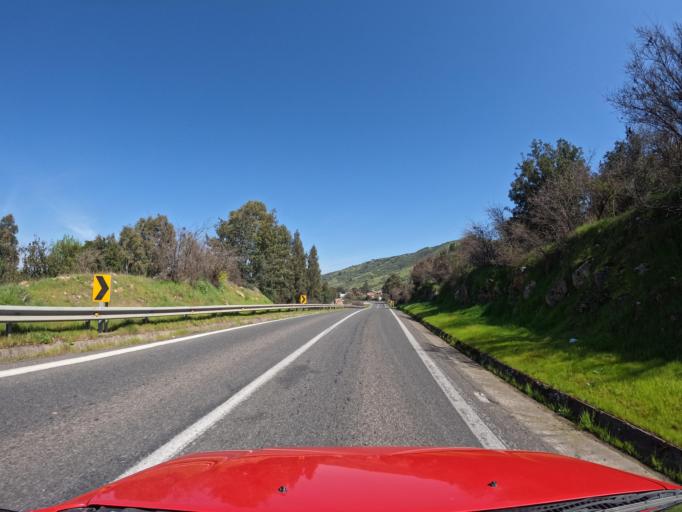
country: CL
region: Maule
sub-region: Provincia de Talca
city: Talca
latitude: -35.0790
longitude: -71.6328
